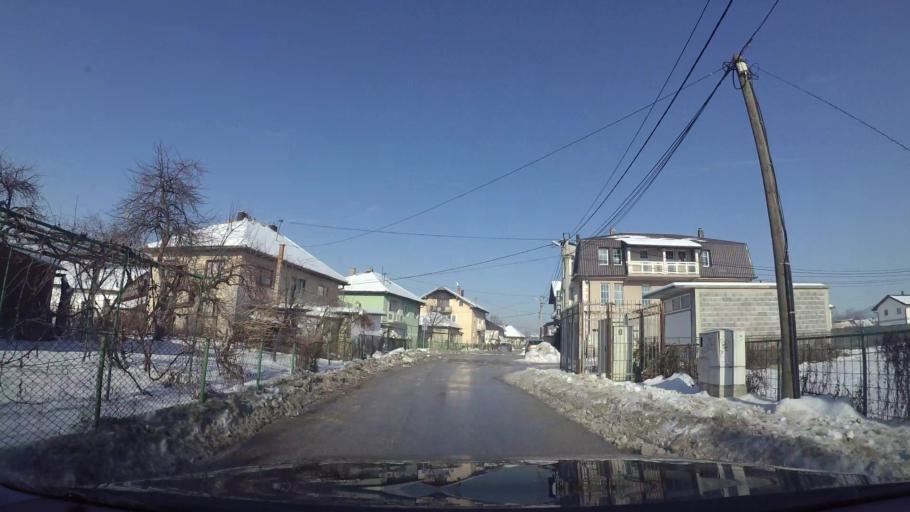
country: BA
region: Federation of Bosnia and Herzegovina
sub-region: Kanton Sarajevo
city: Sarajevo
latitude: 43.8188
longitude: 18.3215
